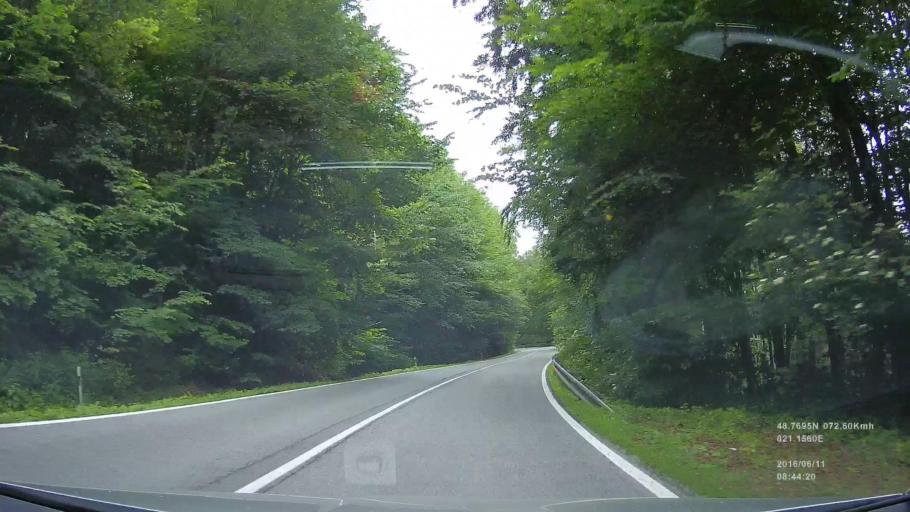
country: SK
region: Kosicky
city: Kosice
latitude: 48.7711
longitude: 21.1619
